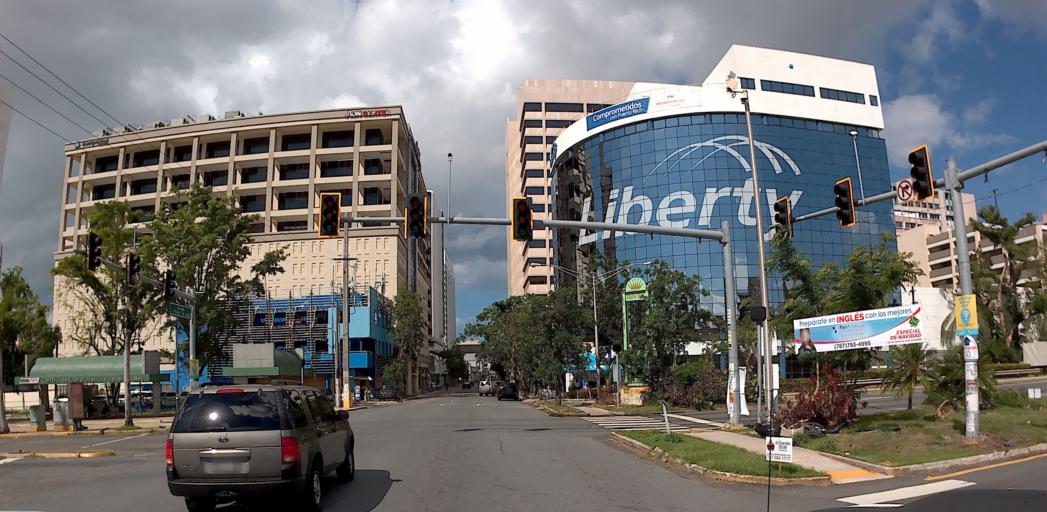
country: PR
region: Catano
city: Catano
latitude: 18.4235
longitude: -66.0572
